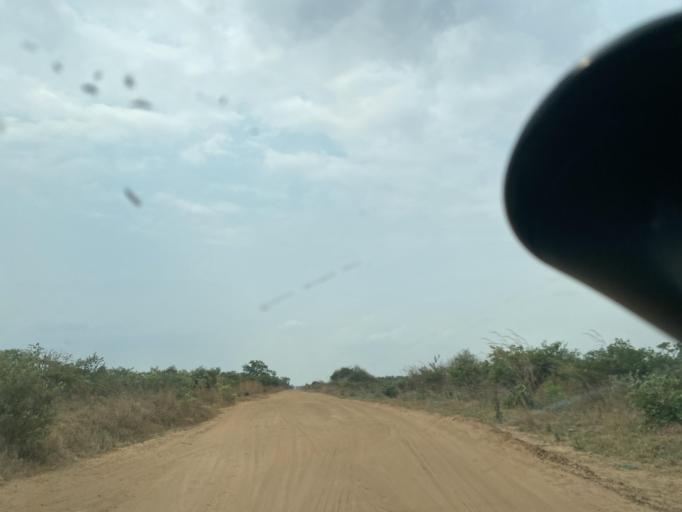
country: ZM
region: Lusaka
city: Lusaka
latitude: -15.2047
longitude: 28.3406
